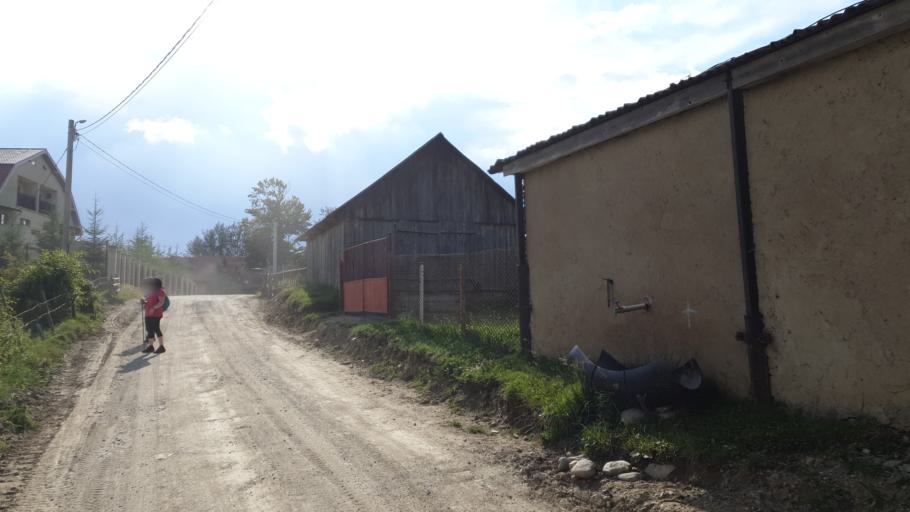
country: RO
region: Hunedoara
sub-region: Oras Petrila
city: Petrila
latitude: 45.3904
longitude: 23.4444
